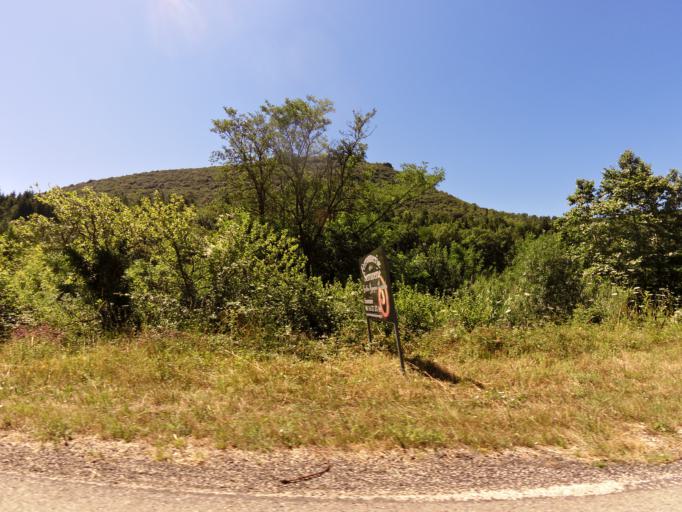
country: FR
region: Languedoc-Roussillon
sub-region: Departement du Gard
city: Saint-Jean-du-Gard
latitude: 44.0978
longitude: 3.9044
